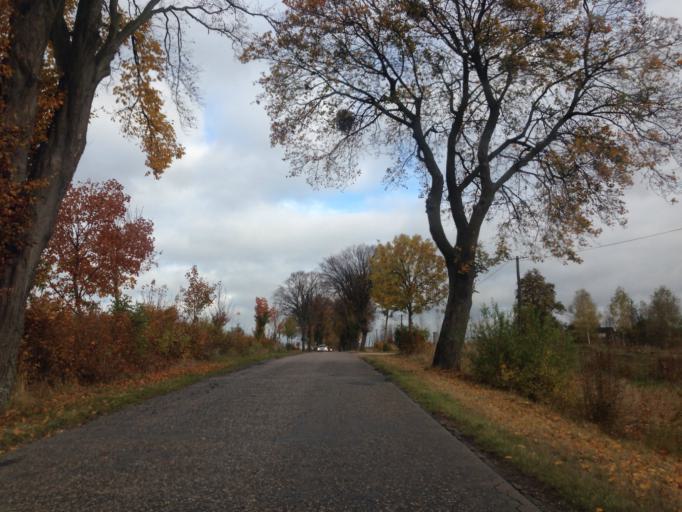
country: PL
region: Kujawsko-Pomorskie
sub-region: Powiat brodnicki
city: Gorzno
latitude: 53.2153
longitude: 19.6349
